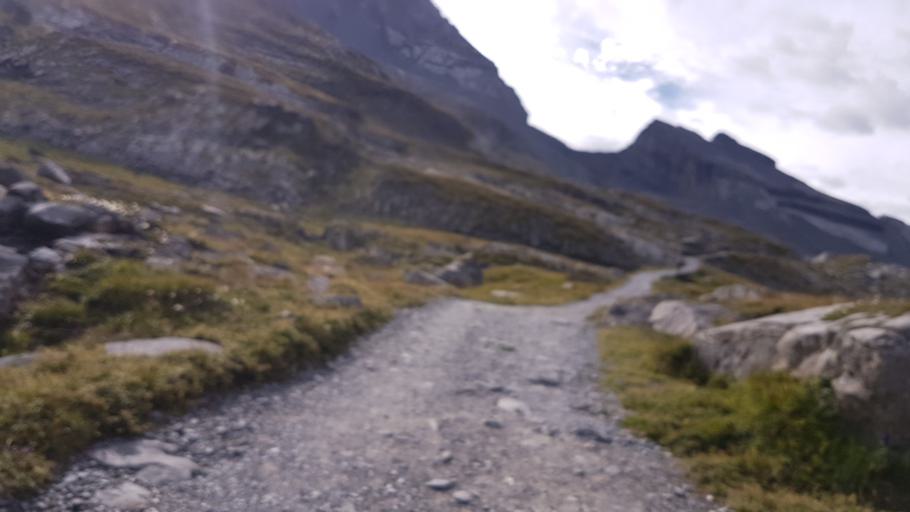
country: CH
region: Valais
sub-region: Leuk District
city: Leukerbad
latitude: 46.4230
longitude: 7.6227
